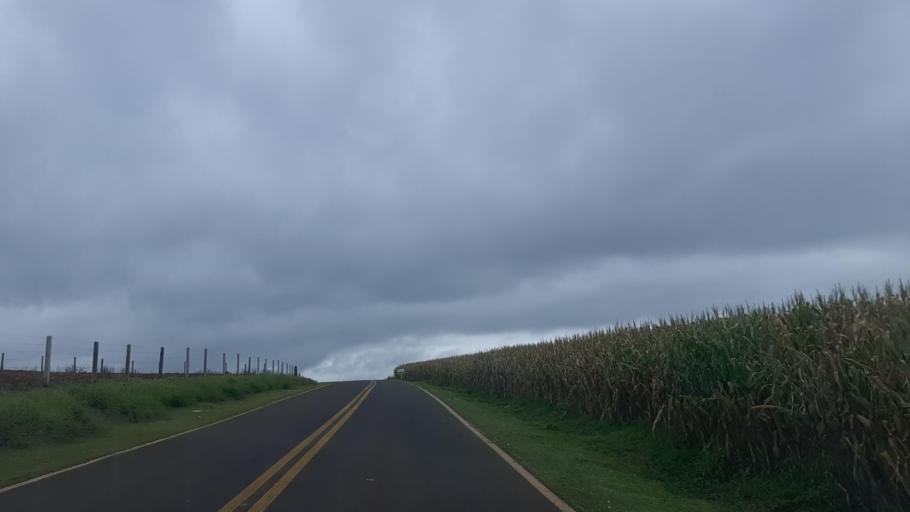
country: BR
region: Parana
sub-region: Ampere
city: Ampere
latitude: -25.9491
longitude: -53.4583
